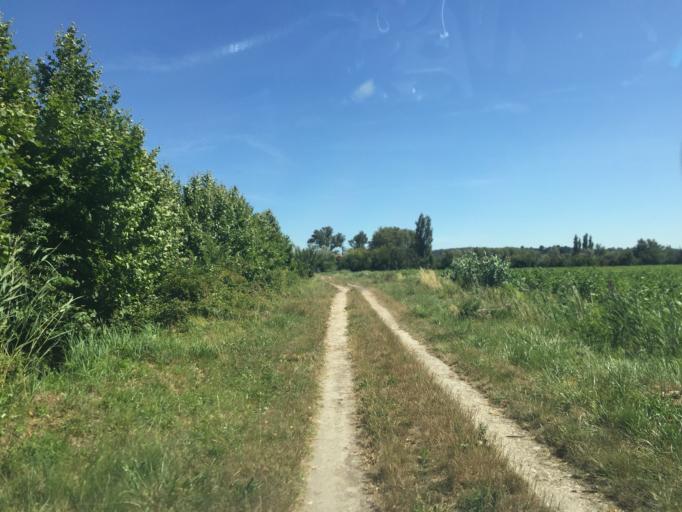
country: FR
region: Provence-Alpes-Cote d'Azur
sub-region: Departement du Vaucluse
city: Bedarrides
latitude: 44.0486
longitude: 4.8983
